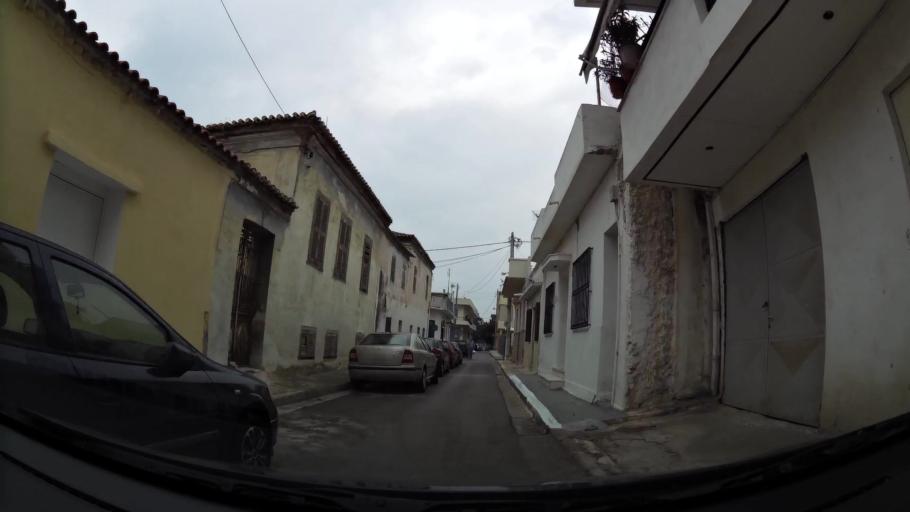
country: GR
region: Attica
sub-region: Nomos Attikis
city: Piraeus
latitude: 37.9551
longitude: 23.6461
